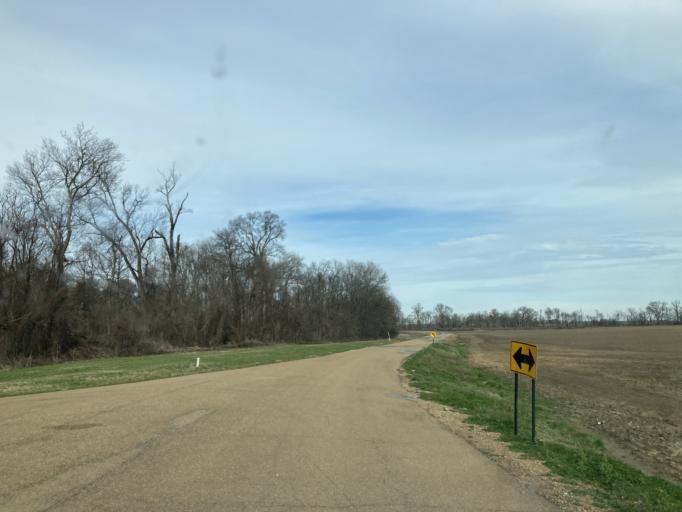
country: US
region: Mississippi
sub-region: Humphreys County
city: Belzoni
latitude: 33.1171
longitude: -90.6132
